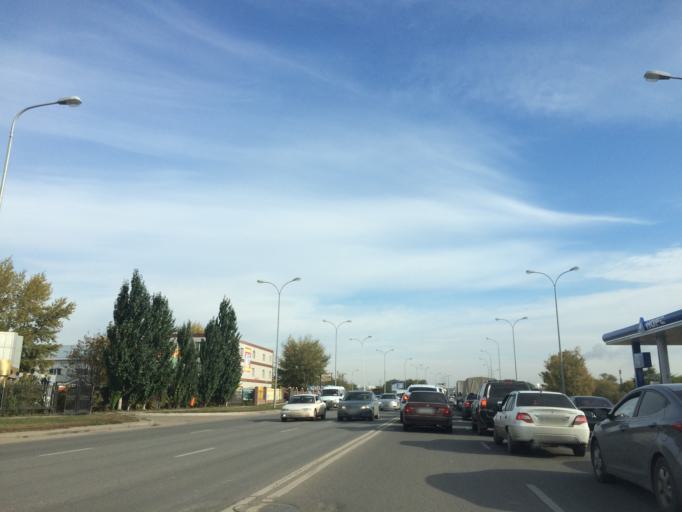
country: KZ
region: Astana Qalasy
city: Astana
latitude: 51.1667
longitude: 71.4765
